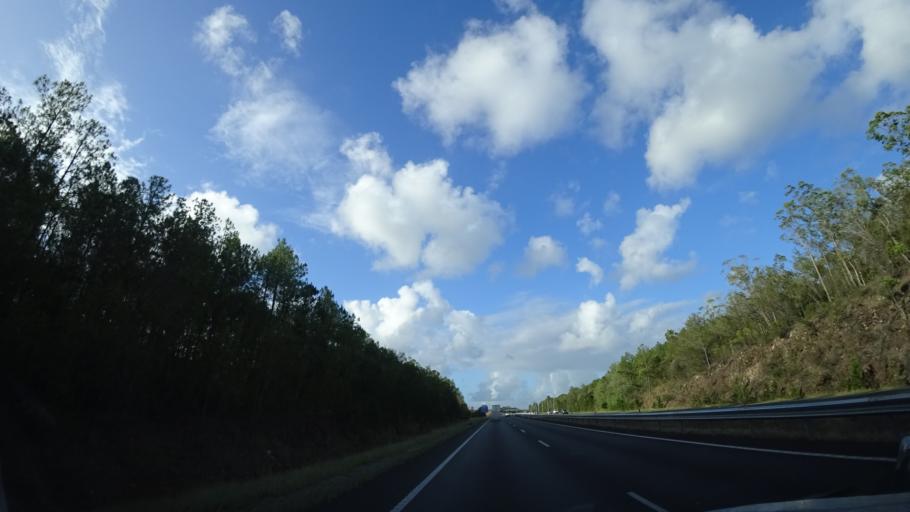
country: AU
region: Queensland
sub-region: Moreton Bay
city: Caboolture
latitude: -26.9263
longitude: 152.9937
